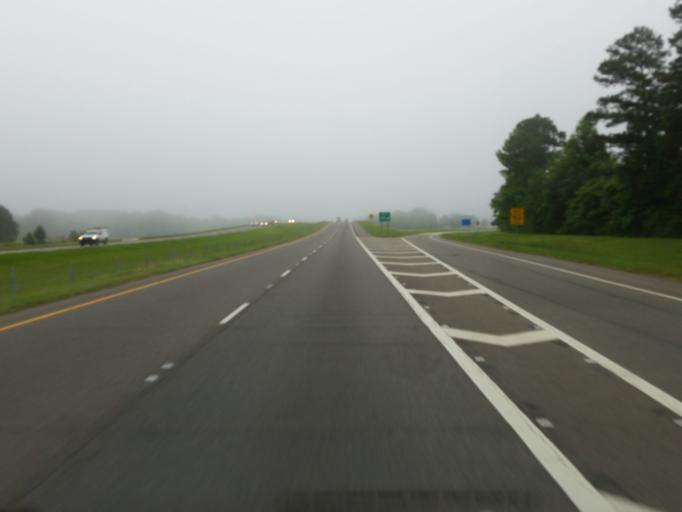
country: US
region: Louisiana
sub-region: Bossier Parish
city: Haughton
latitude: 32.5783
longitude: -93.4370
